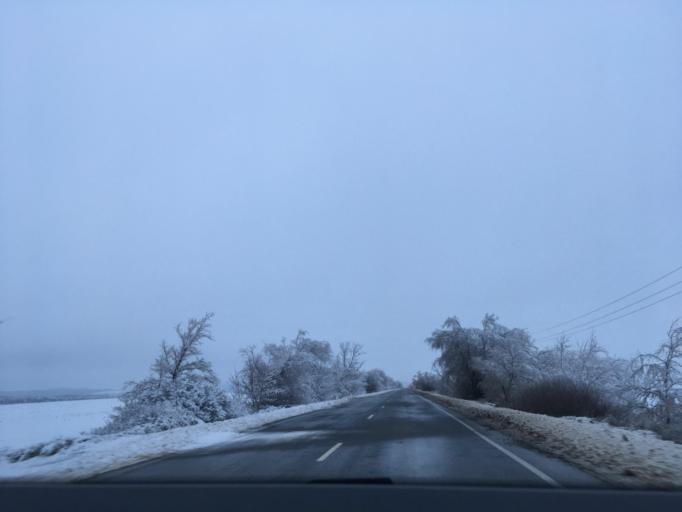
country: RU
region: Voronezj
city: Verkhniy Mamon
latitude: 50.0217
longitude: 40.0964
